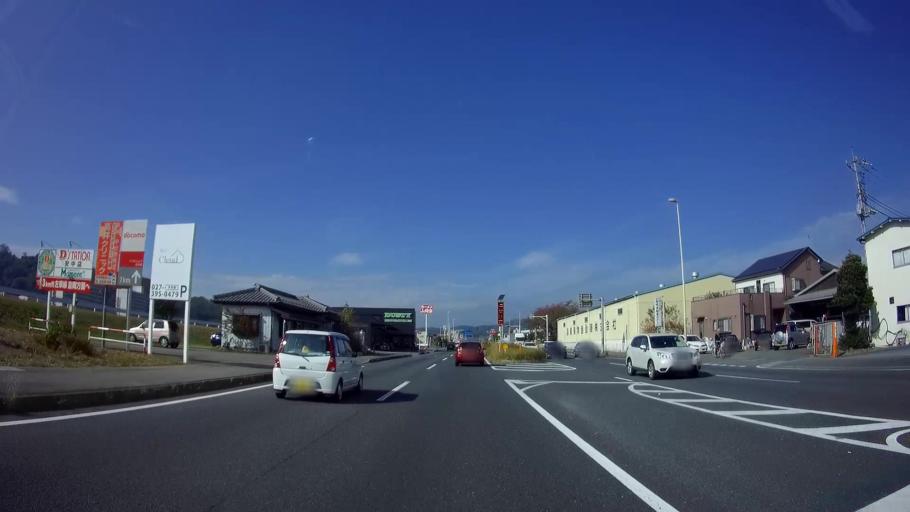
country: JP
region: Gunma
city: Annaka
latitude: 36.3340
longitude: 138.9486
